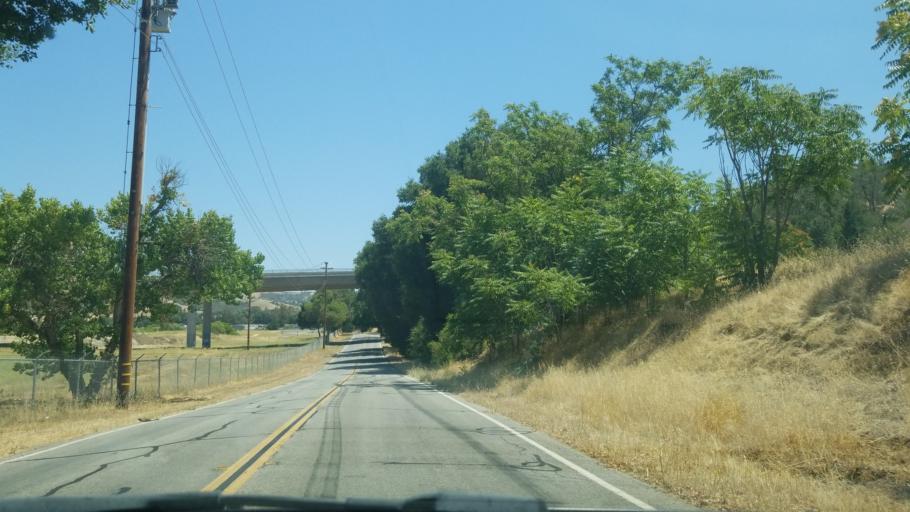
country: US
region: California
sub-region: San Luis Obispo County
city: Atascadero
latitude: 35.5003
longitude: -120.6606
